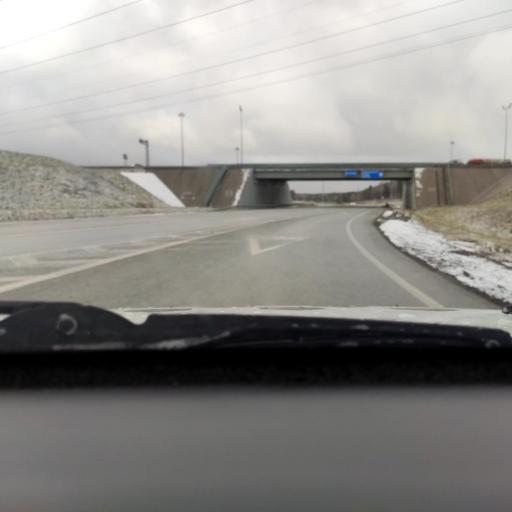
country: RU
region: Perm
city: Novyye Lyady
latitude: 58.0448
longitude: 56.4327
